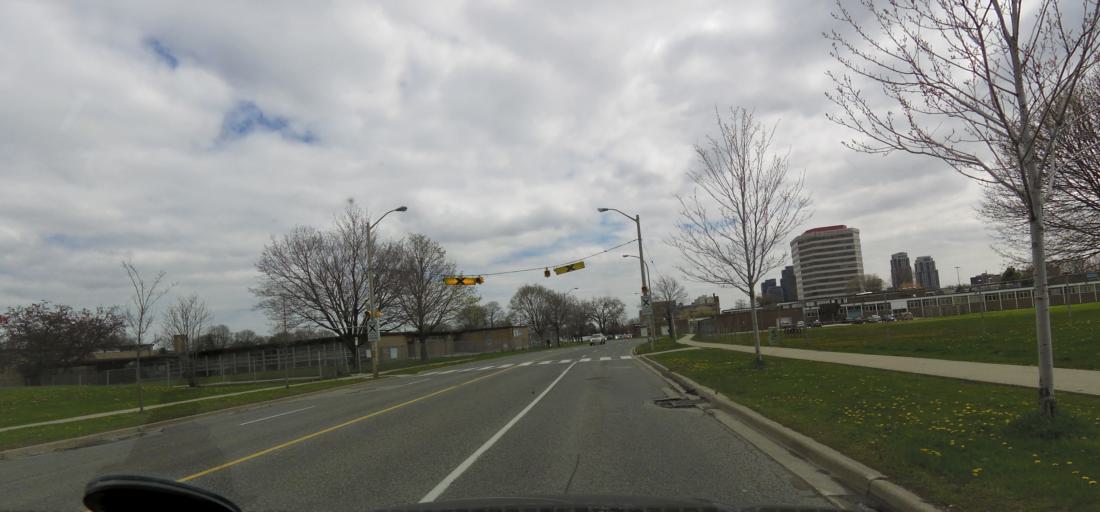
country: CA
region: Ontario
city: Etobicoke
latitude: 43.6507
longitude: -79.5624
